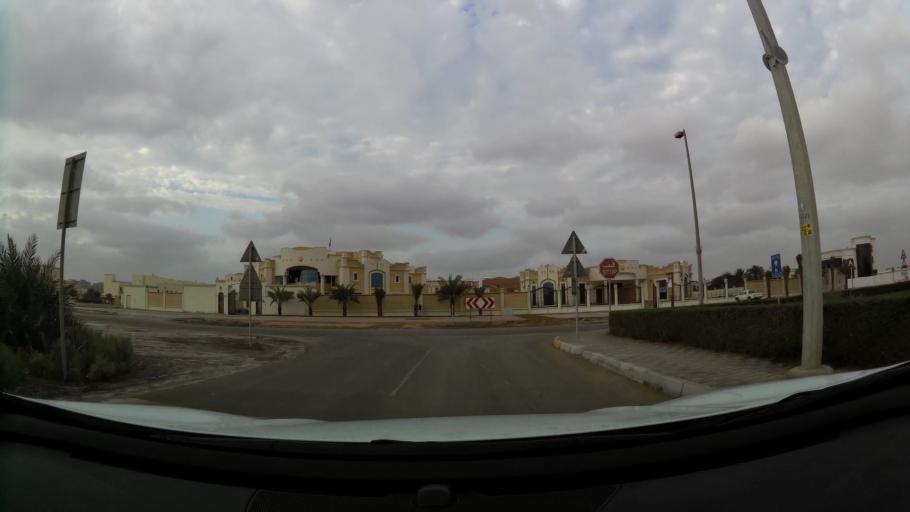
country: AE
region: Abu Dhabi
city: Abu Dhabi
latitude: 24.3637
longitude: 54.5485
